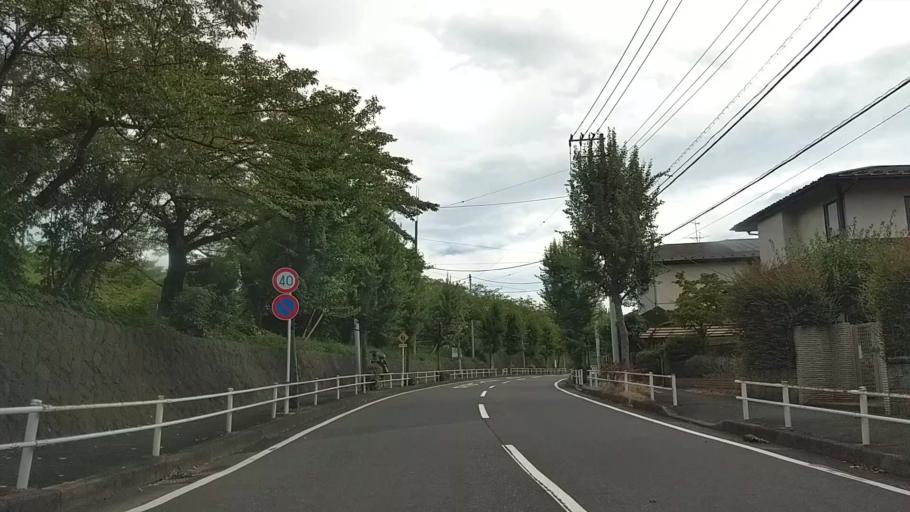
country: JP
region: Tokyo
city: Hachioji
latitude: 35.6313
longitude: 139.3580
